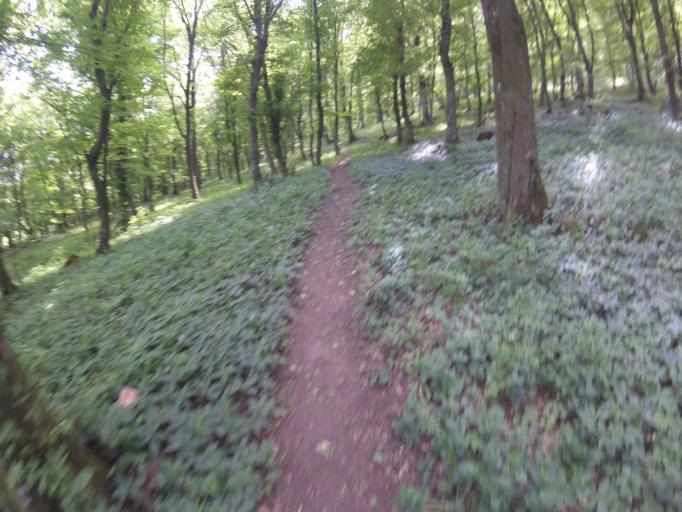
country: SK
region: Kosicky
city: Medzev
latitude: 48.6219
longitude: 20.8599
